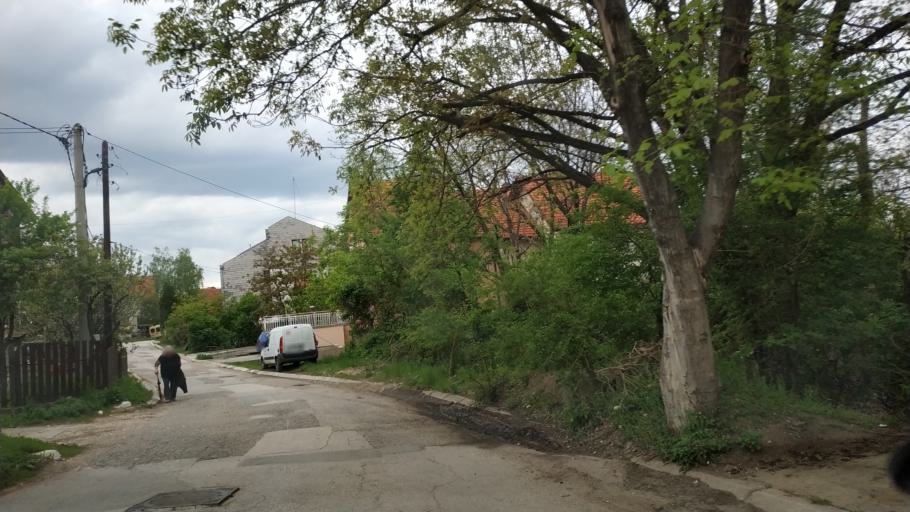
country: RS
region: Central Serbia
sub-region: Zajecarski Okrug
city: Soko Banja
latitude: 43.6427
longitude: 21.8699
